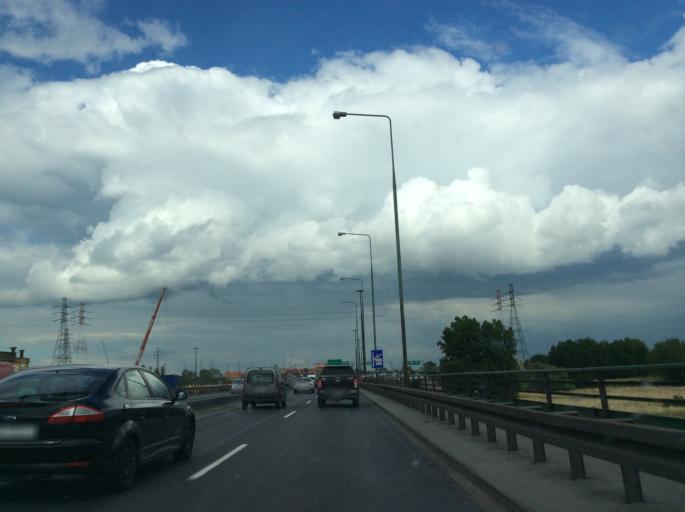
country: PL
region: Masovian Voivodeship
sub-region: Warszawa
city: Zoliborz
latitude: 52.2876
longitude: 20.9964
